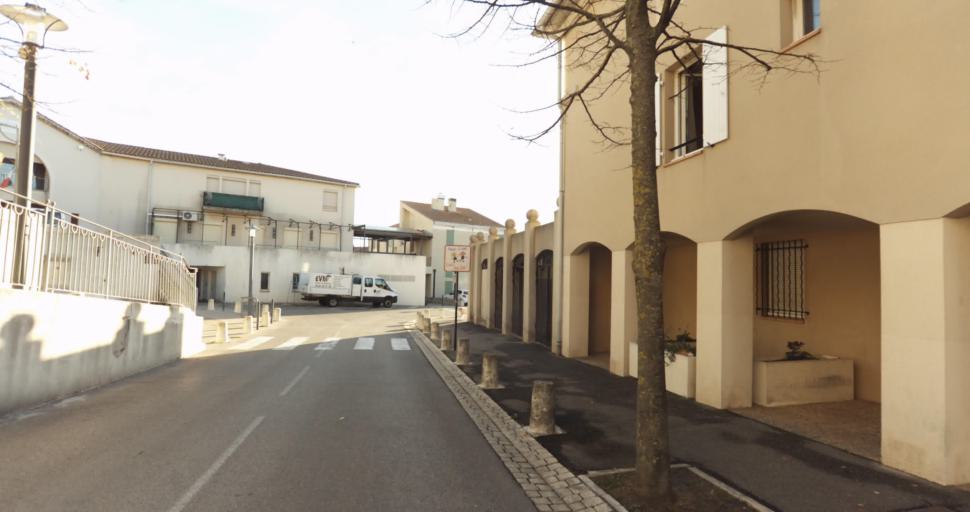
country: FR
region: Provence-Alpes-Cote d'Azur
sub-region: Departement des Bouches-du-Rhone
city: Venelles
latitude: 43.5973
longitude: 5.4821
